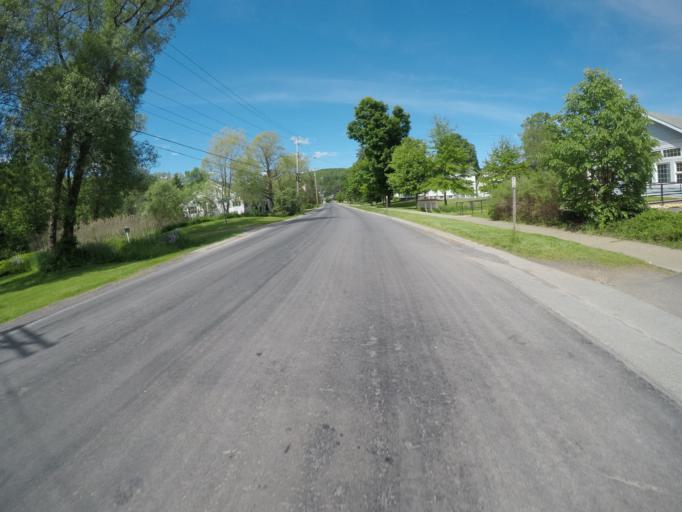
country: US
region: New York
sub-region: Delaware County
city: Delhi
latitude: 42.1858
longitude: -74.7880
